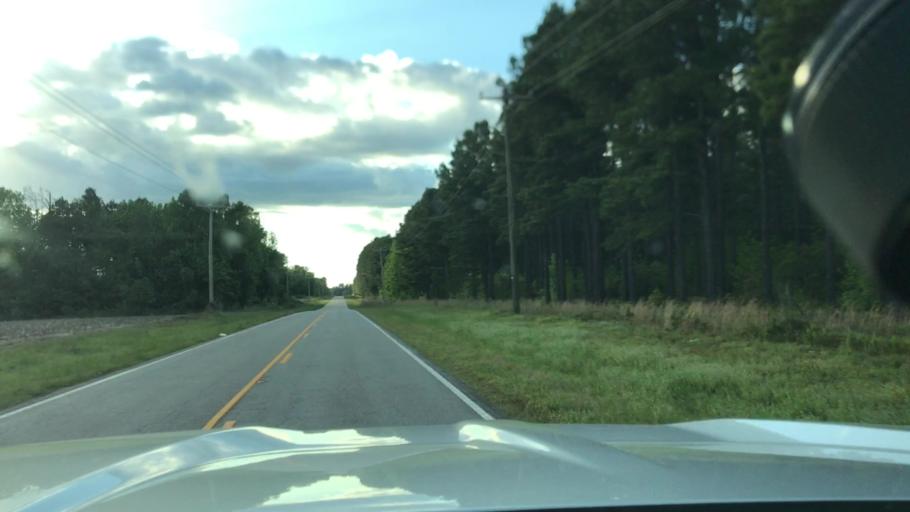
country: US
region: South Carolina
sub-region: Bamberg County
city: Denmark
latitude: 33.4664
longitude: -81.1610
